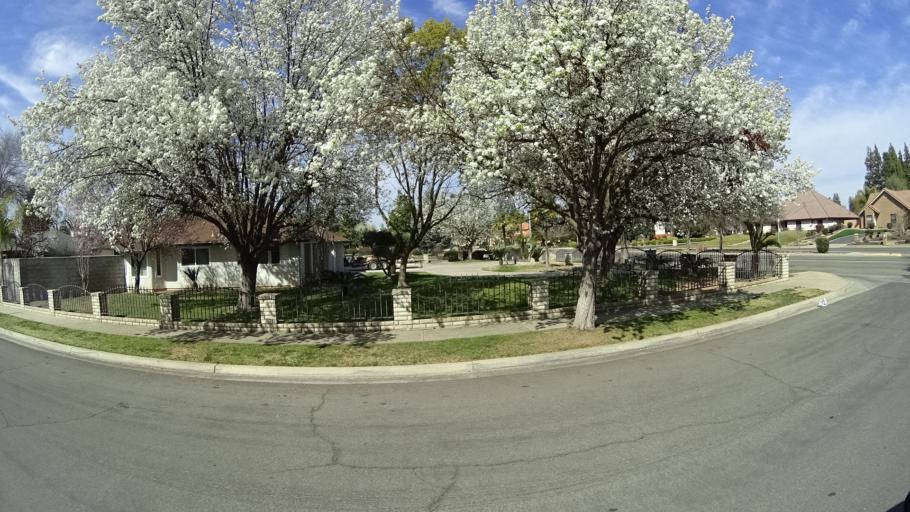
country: US
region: California
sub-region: Fresno County
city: Clovis
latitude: 36.8556
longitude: -119.7756
